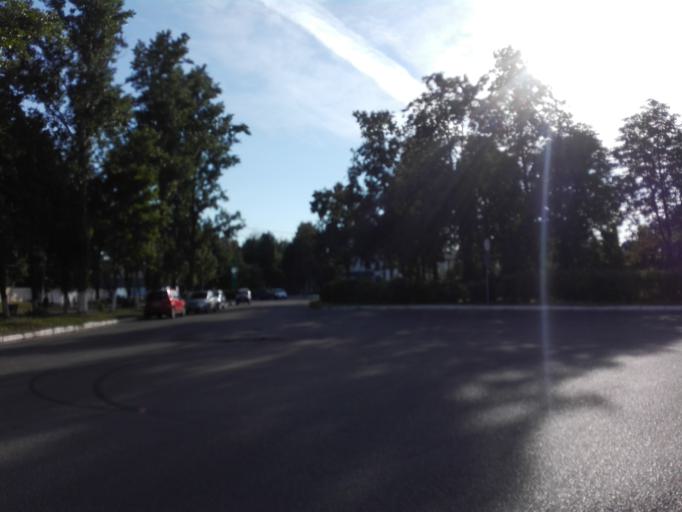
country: RU
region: Orjol
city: Orel
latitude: 52.9506
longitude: 36.0503
